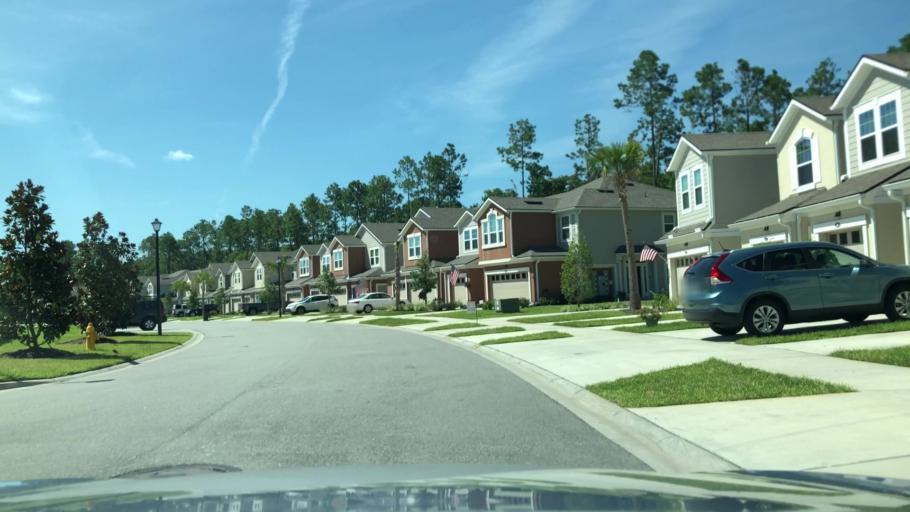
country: US
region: Florida
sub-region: Saint Johns County
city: Fruit Cove
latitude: 30.0724
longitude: -81.5346
